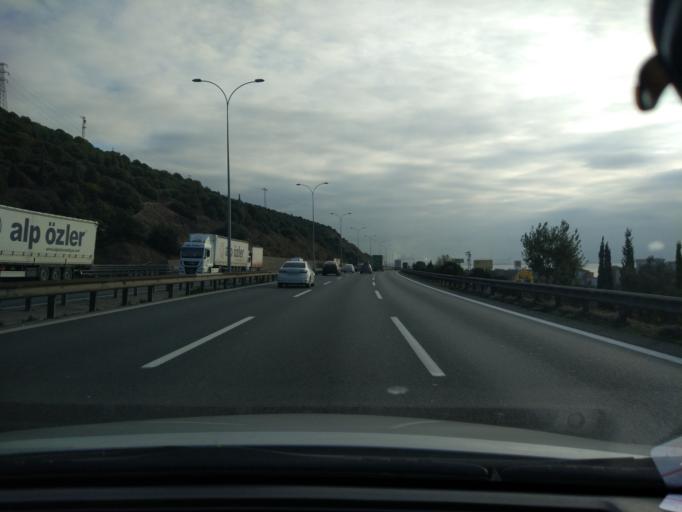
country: TR
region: Kocaeli
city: Hereke
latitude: 40.7800
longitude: 29.6681
